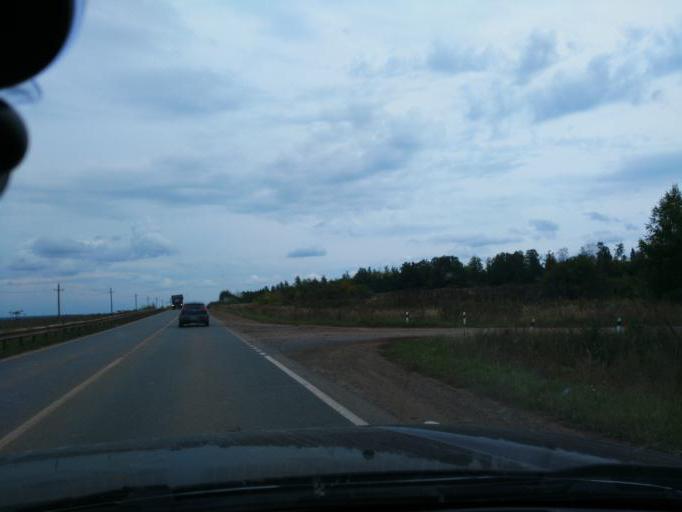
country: RU
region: Perm
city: Chernushka
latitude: 56.5101
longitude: 55.9469
